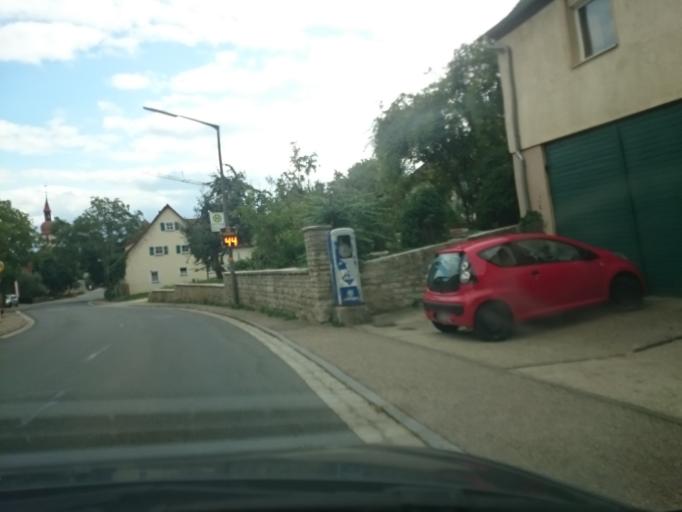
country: DE
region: Bavaria
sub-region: Regierungsbezirk Mittelfranken
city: Thalmassing
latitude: 49.1246
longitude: 11.2689
